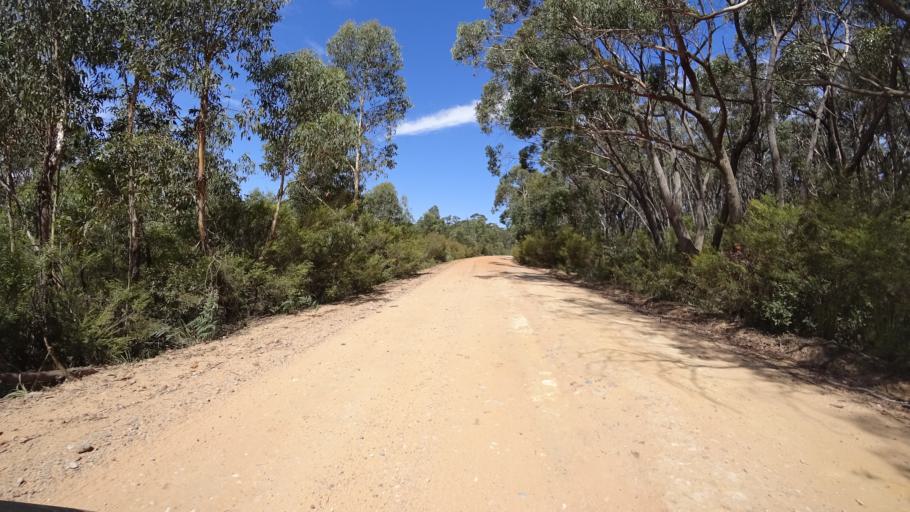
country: AU
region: New South Wales
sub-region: Lithgow
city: Lithgow
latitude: -33.3180
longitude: 150.2465
